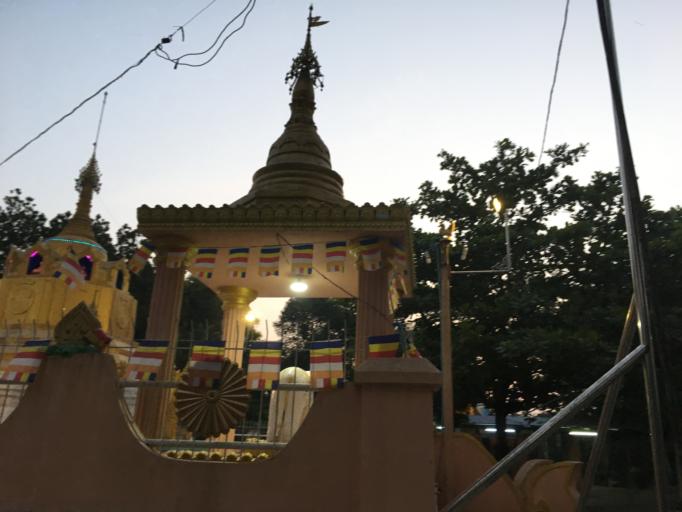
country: MM
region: Mon
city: Mawlamyine
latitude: 16.4821
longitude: 97.6284
